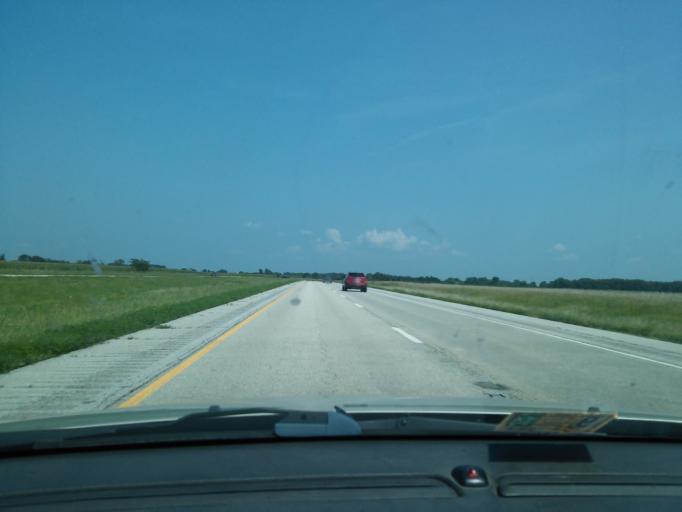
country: US
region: Illinois
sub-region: Sangamon County
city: New Berlin
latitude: 39.7382
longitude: -89.9777
